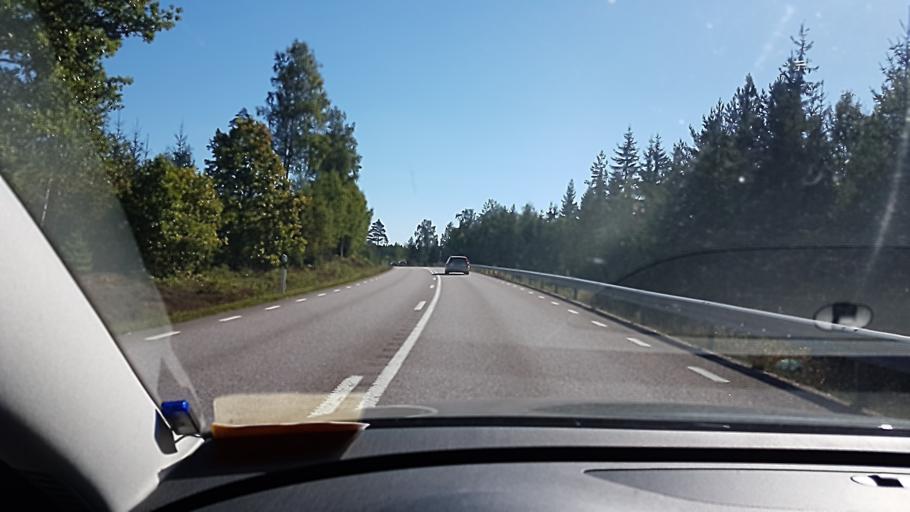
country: SE
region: Kronoberg
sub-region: Lessebo Kommun
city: Lessebo
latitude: 56.7814
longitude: 15.2022
